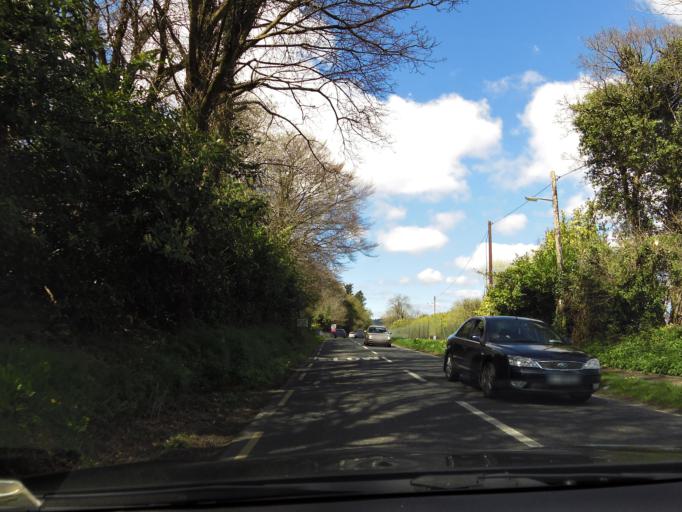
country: IE
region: Leinster
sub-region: Wicklow
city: Arklow
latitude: 52.8027
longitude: -6.1748
